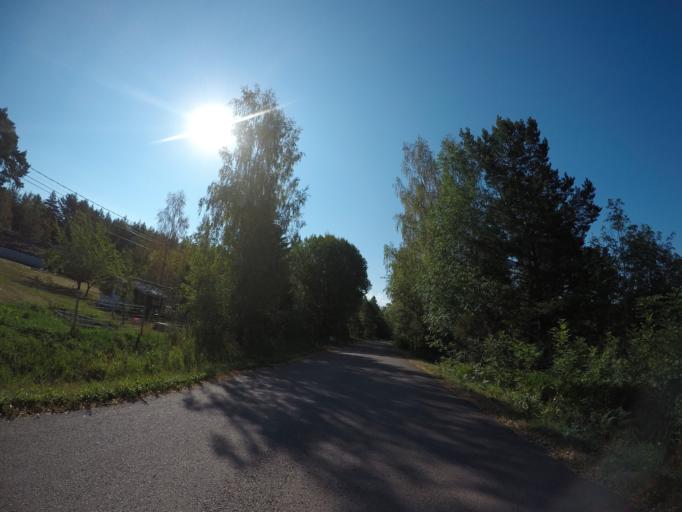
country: AX
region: Alands landsbygd
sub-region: Finstroem
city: Finstroem
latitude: 60.3300
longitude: 19.9118
